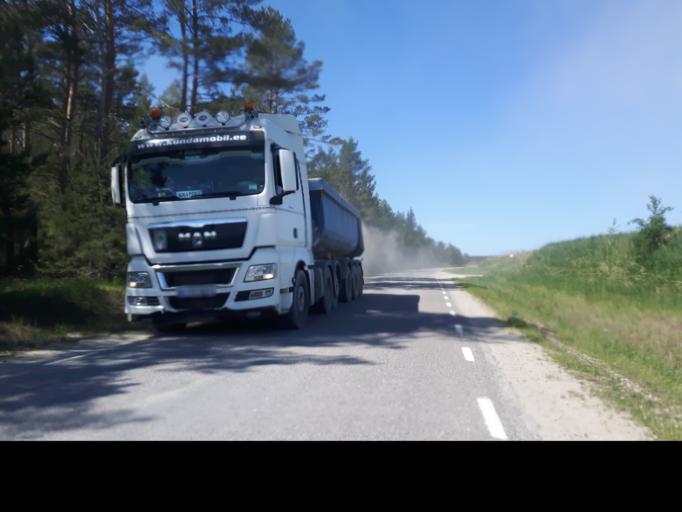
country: EE
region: Laeaene-Virumaa
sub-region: Viru-Nigula vald
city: Kunda
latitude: 59.5049
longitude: 26.4768
